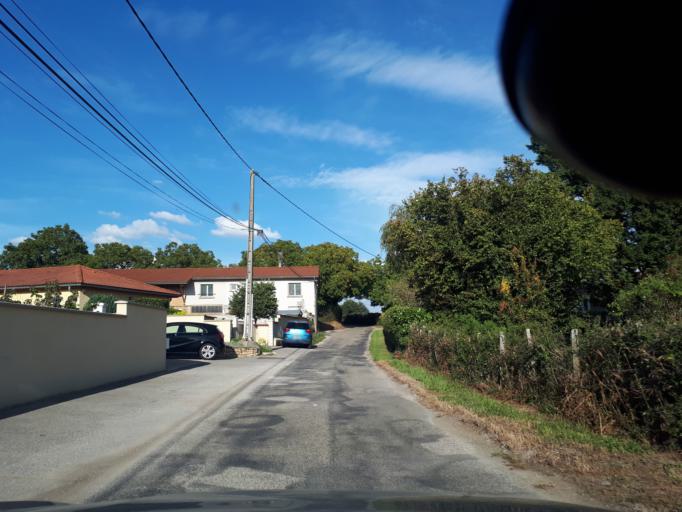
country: FR
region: Rhone-Alpes
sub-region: Departement de l'Isere
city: Maubec
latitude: 45.5206
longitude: 5.2493
